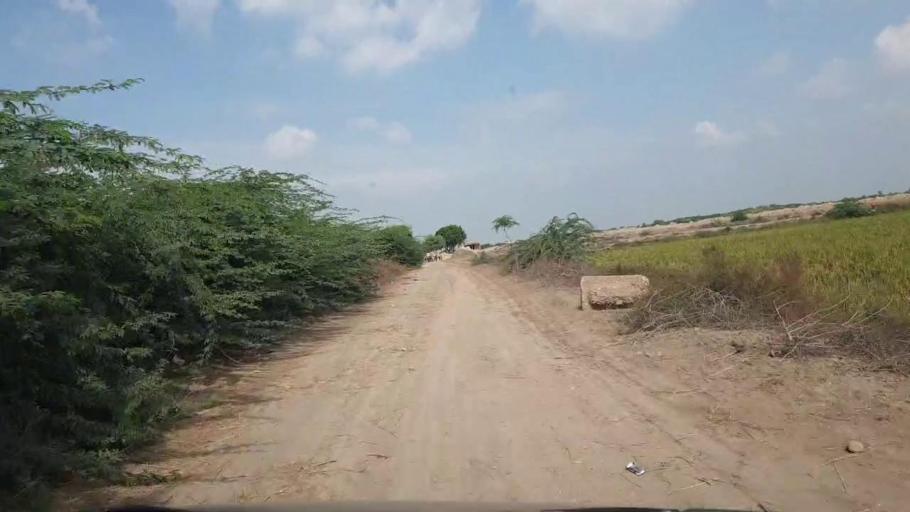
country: PK
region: Sindh
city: Badin
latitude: 24.4709
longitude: 68.5902
